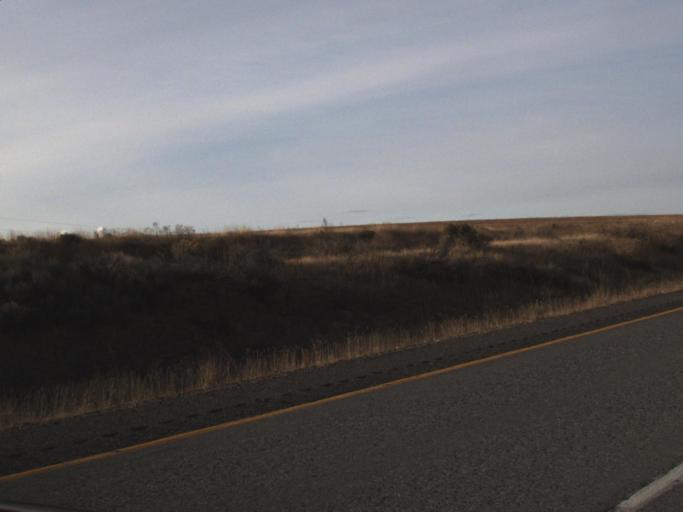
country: US
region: Washington
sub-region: Benton County
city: Highland
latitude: 46.0682
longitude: -119.2234
